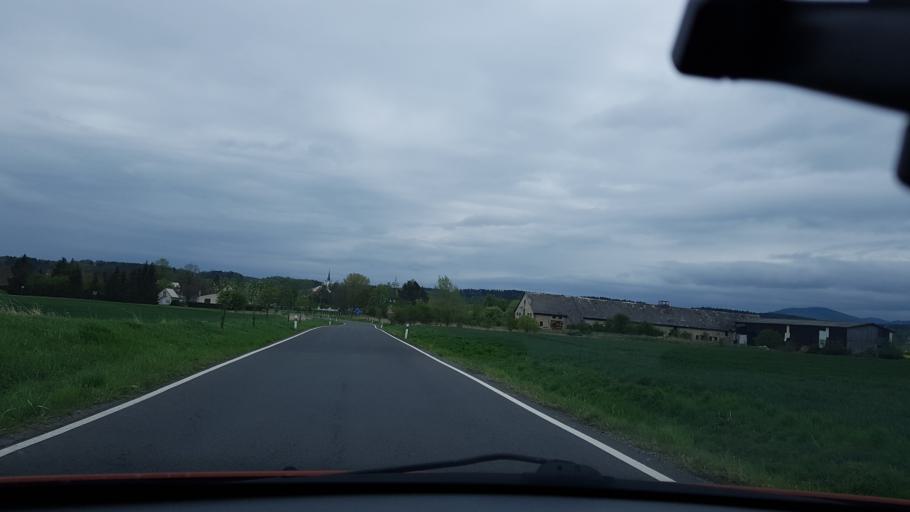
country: CZ
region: Olomoucky
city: Vidnava
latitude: 50.3754
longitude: 17.1756
